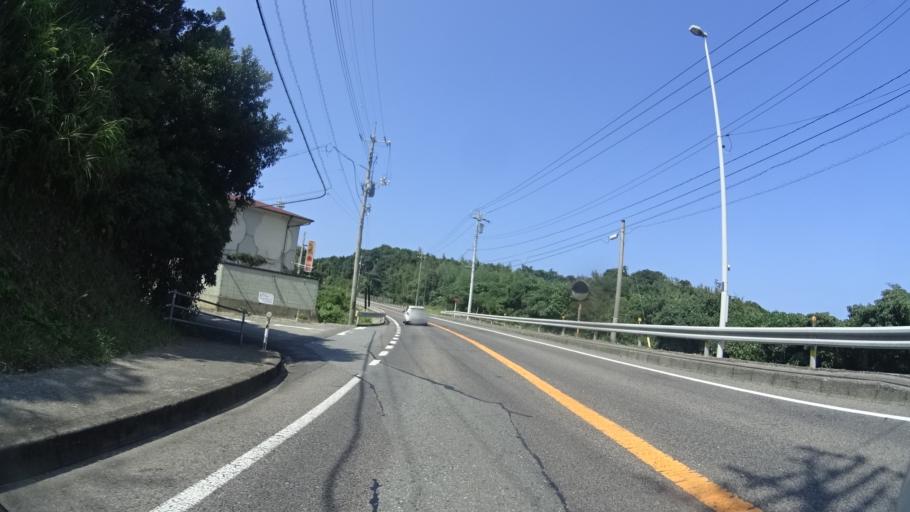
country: JP
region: Shimane
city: Masuda
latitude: 34.6745
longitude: 131.7213
